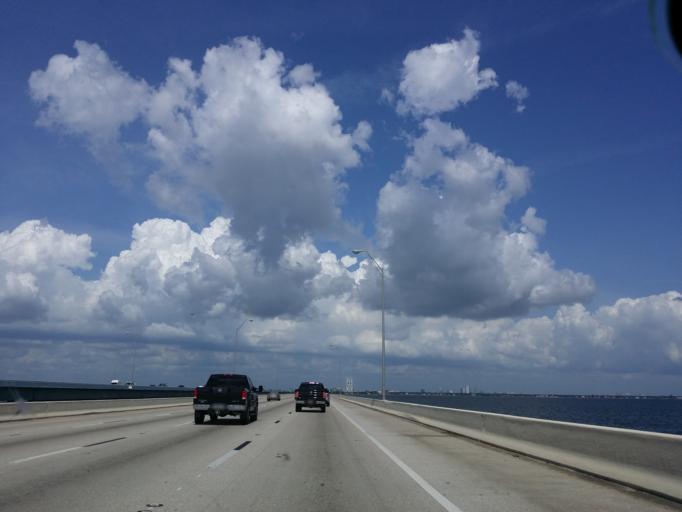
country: US
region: Florida
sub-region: Pinellas County
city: Gandy
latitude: 27.9304
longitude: -82.5798
